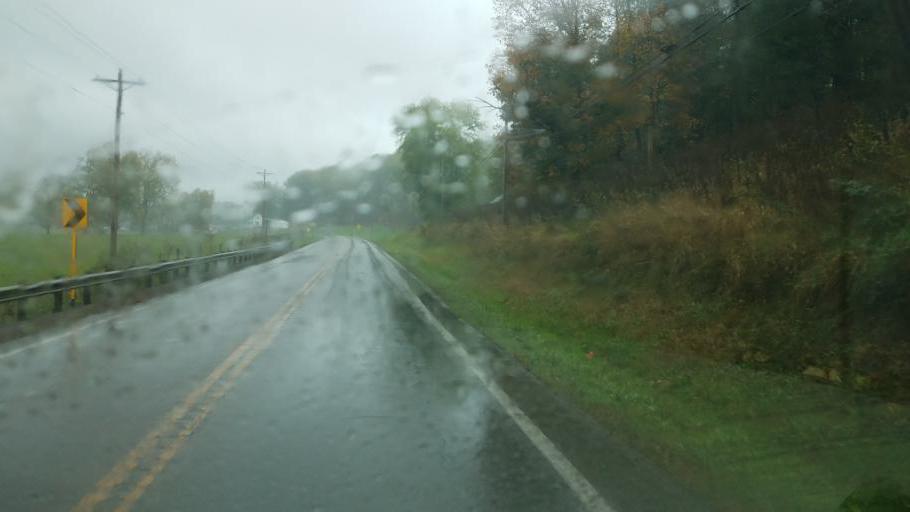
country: US
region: Ohio
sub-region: Holmes County
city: Millersburg
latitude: 40.5752
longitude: -81.9228
